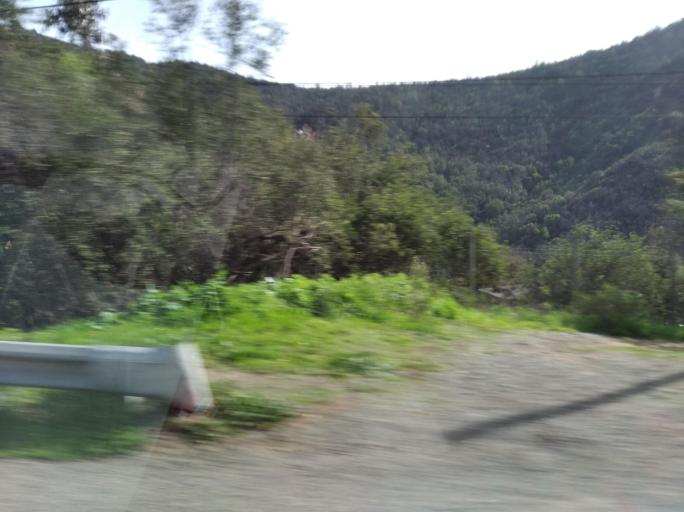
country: CL
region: Valparaiso
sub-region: Provincia de Marga Marga
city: Limache
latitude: -33.0611
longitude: -71.0586
